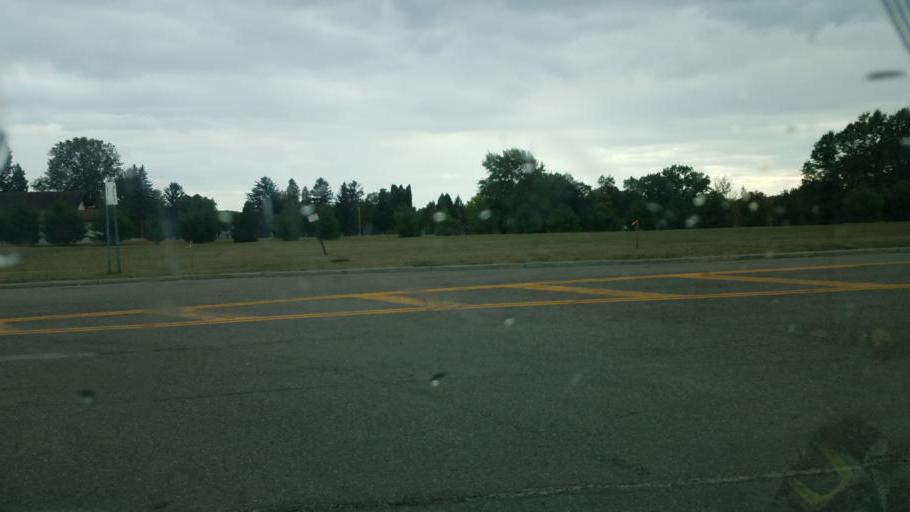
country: US
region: Ohio
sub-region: Portage County
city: Brimfield
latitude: 41.1044
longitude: -81.3482
